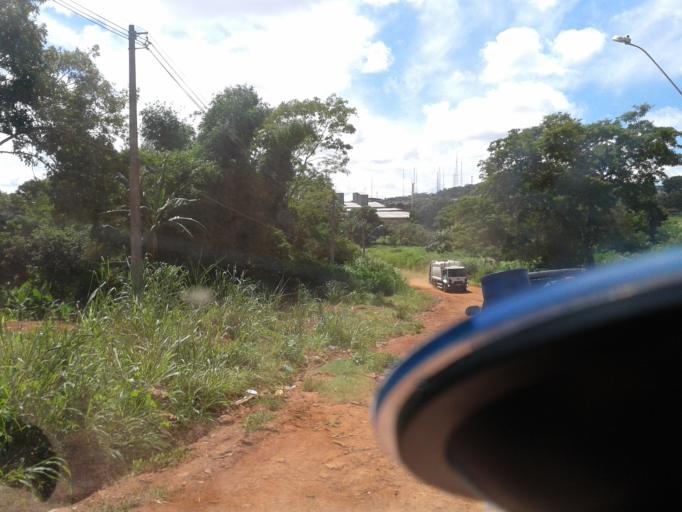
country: BR
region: Goias
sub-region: Goiania
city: Goiania
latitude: -16.6489
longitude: -49.3546
